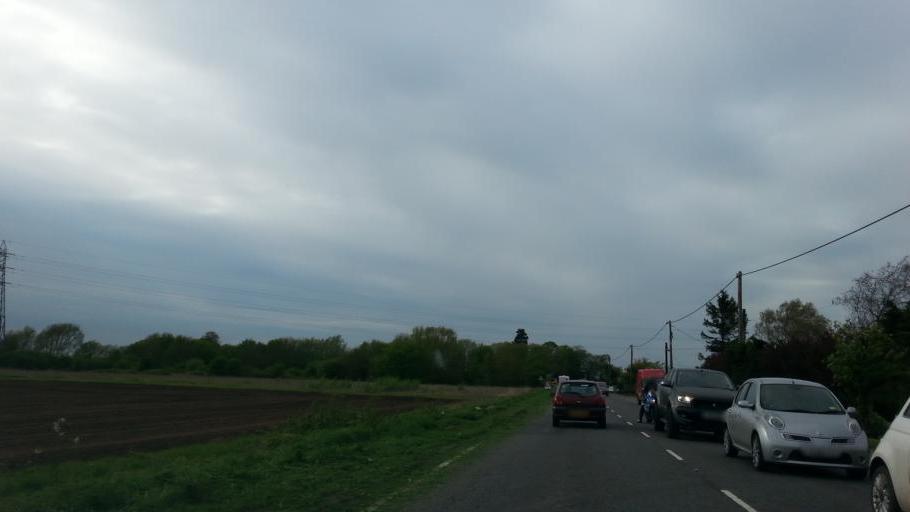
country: GB
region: England
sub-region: Cambridgeshire
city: March
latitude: 52.5725
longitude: 0.0580
